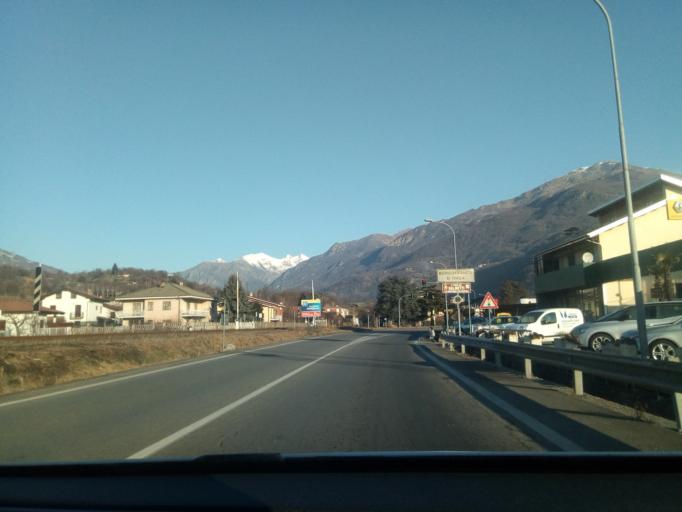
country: IT
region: Piedmont
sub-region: Provincia di Torino
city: Borgofranco d'Ivrea
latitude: 45.5065
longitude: 7.8561
